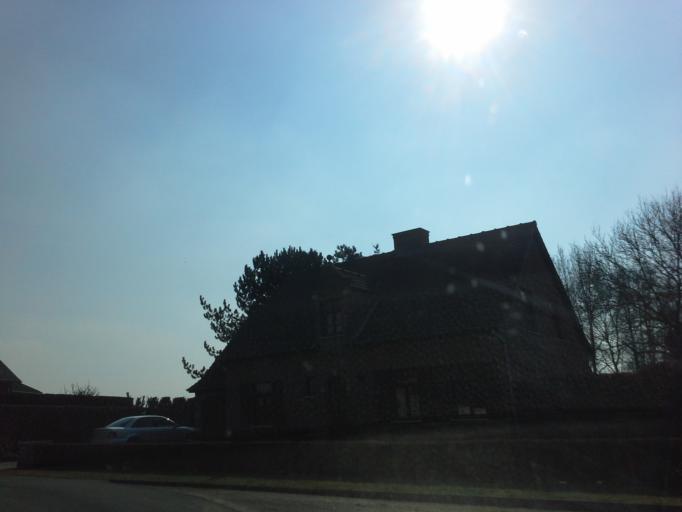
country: BE
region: Flanders
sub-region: Provincie Antwerpen
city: Meerhout
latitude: 51.1382
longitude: 5.0660
